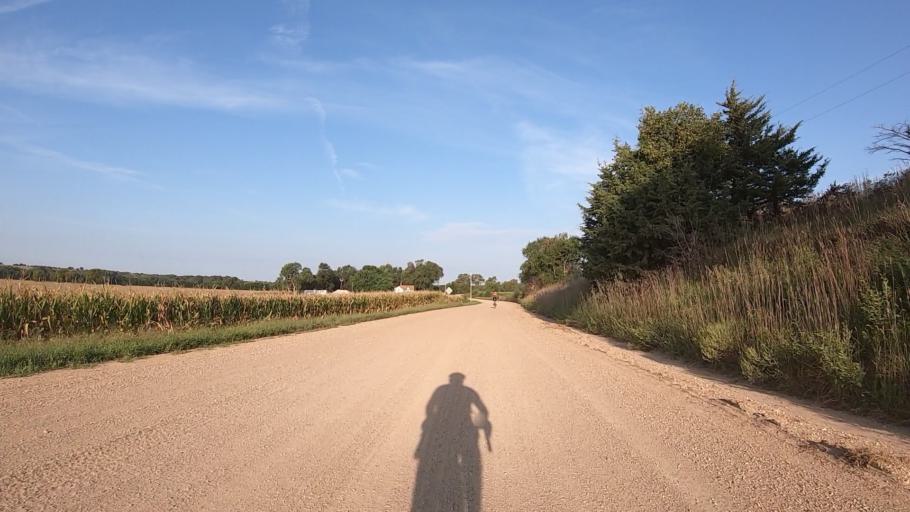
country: US
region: Kansas
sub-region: Marshall County
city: Blue Rapids
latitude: 39.7261
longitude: -96.7896
